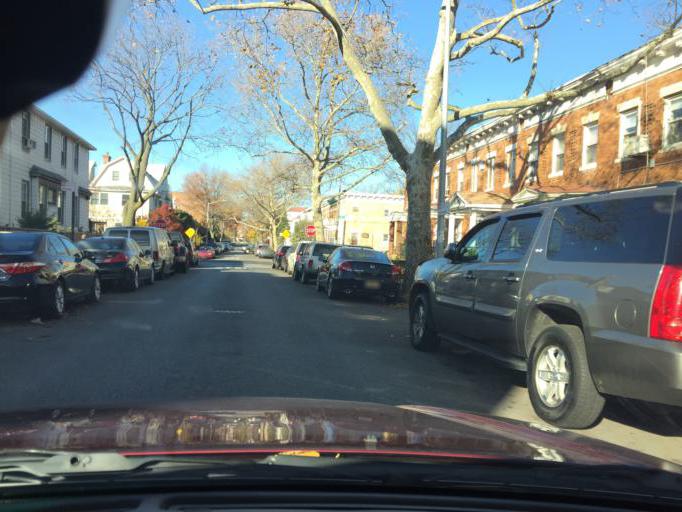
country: US
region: New York
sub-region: Kings County
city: Brooklyn
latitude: 40.6271
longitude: -73.9617
